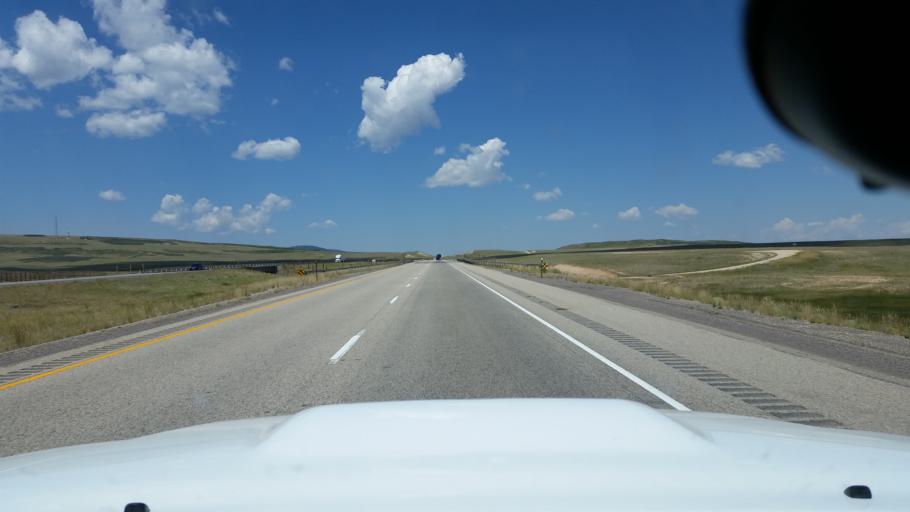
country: US
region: Wyoming
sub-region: Albany County
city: Laramie
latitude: 41.4839
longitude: -106.0231
